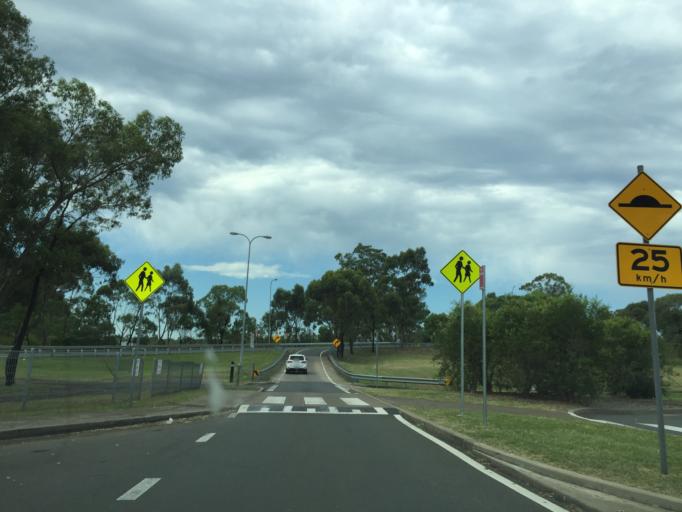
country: AU
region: New South Wales
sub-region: Blacktown
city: Doonside
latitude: -33.8012
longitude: 150.8874
